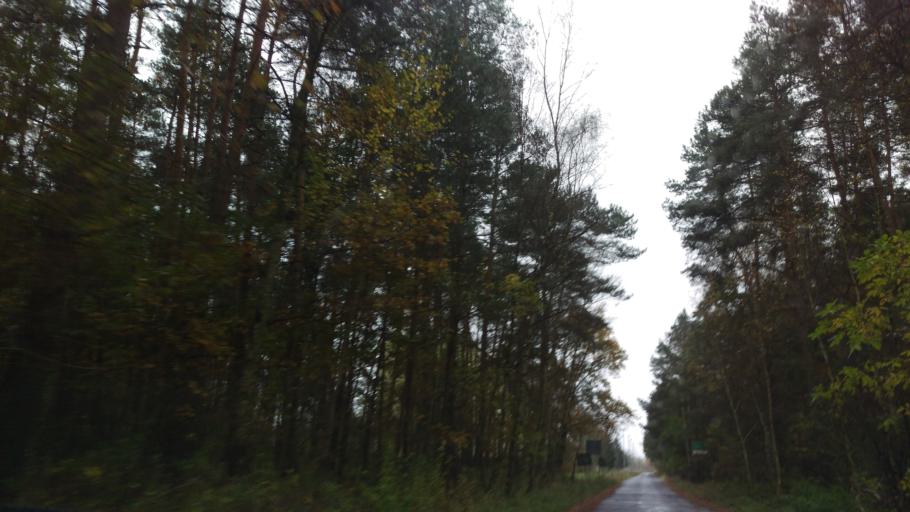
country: PL
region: West Pomeranian Voivodeship
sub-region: Powiat stargardzki
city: Kobylanka
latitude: 53.4051
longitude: 14.7730
